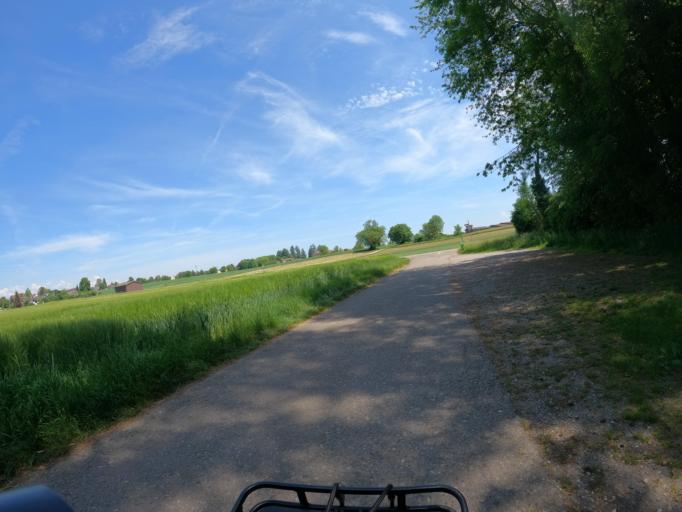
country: DE
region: Baden-Wuerttemberg
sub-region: Freiburg Region
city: Lottstetten
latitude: 47.6321
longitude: 8.5997
